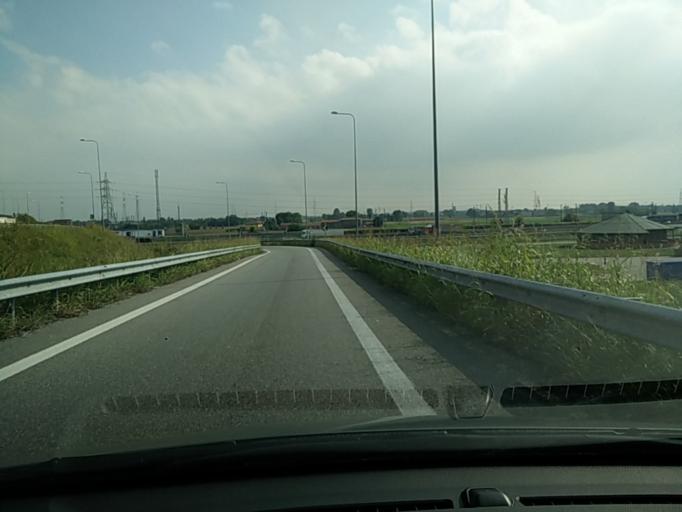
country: IT
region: Lombardy
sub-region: Citta metropolitana di Milano
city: Mesero
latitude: 45.4857
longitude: 8.8473
